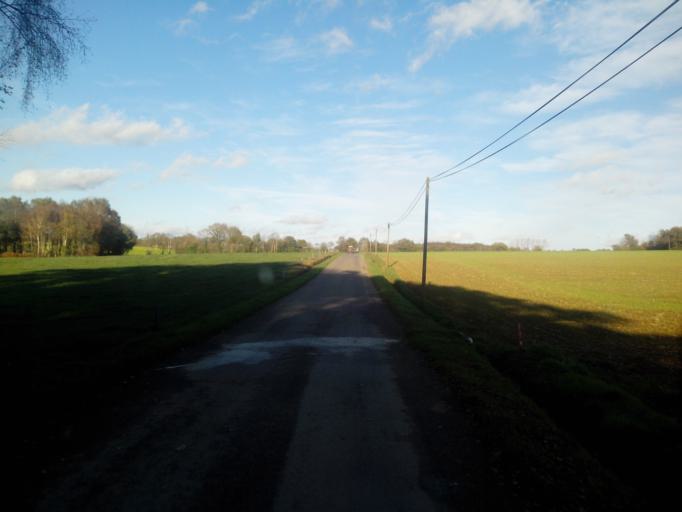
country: FR
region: Brittany
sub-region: Departement du Morbihan
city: Guilliers
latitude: 48.0958
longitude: -2.4062
